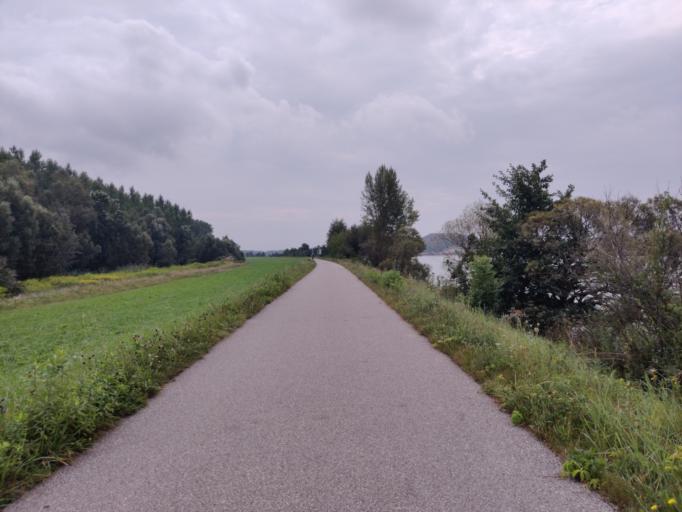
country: AT
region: Upper Austria
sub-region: Politischer Bezirk Urfahr-Umgebung
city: Steyregg
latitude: 48.2812
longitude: 14.3499
